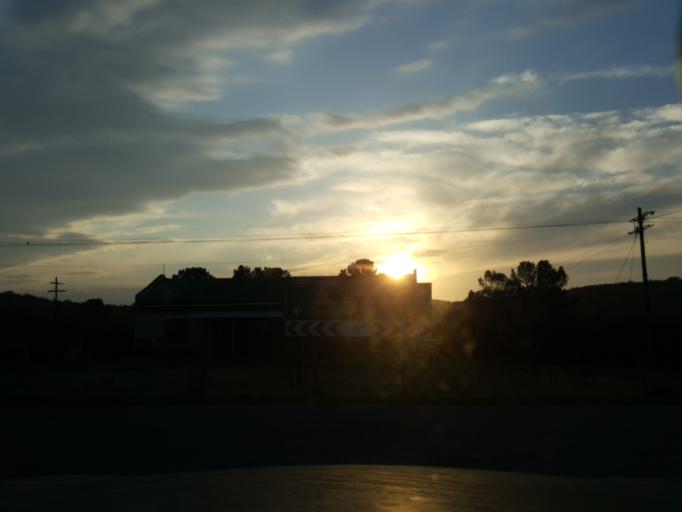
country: ZA
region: Eastern Cape
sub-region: Cacadu District Municipality
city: Grahamstown
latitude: -33.4699
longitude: 26.4806
